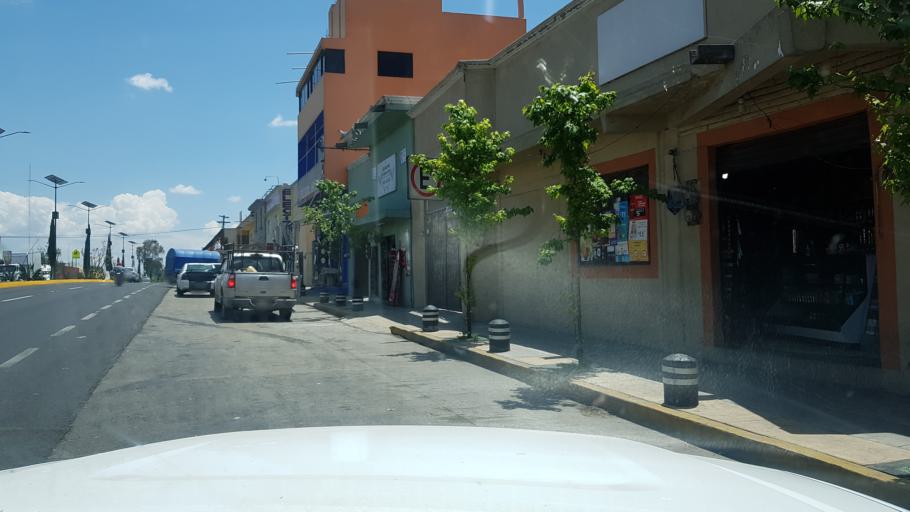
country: MX
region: Hidalgo
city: Calpulalpan
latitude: 19.5921
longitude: -98.5670
